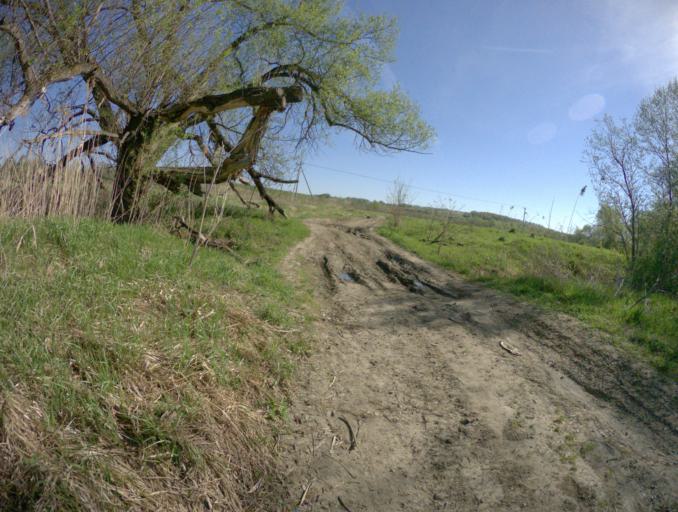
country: RU
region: Vladimir
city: Vladimir
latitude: 56.1959
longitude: 40.3831
